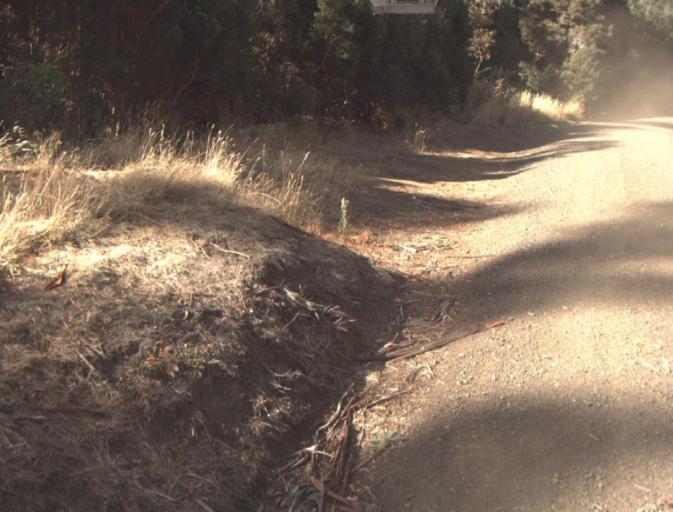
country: AU
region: Tasmania
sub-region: Dorset
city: Bridport
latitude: -41.1543
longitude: 147.2234
